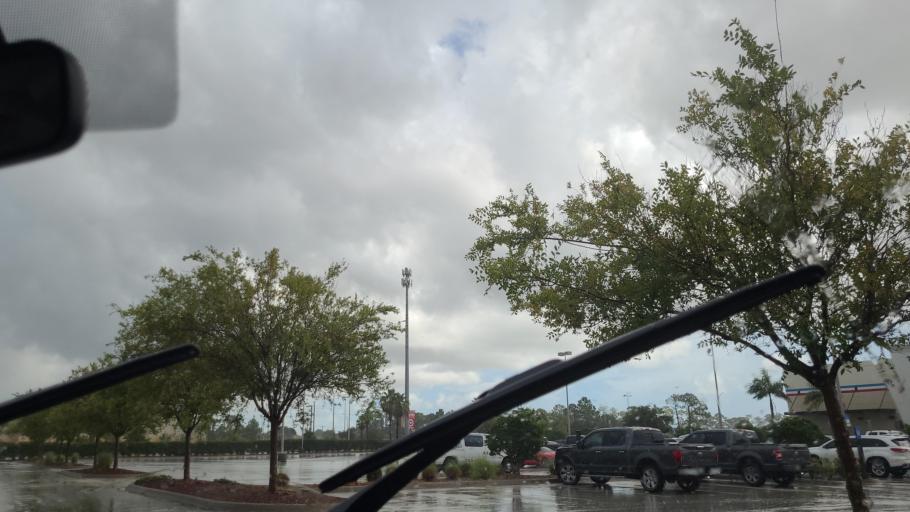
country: US
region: Florida
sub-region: Brevard County
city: West Melbourne
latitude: 28.0396
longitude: -80.6623
